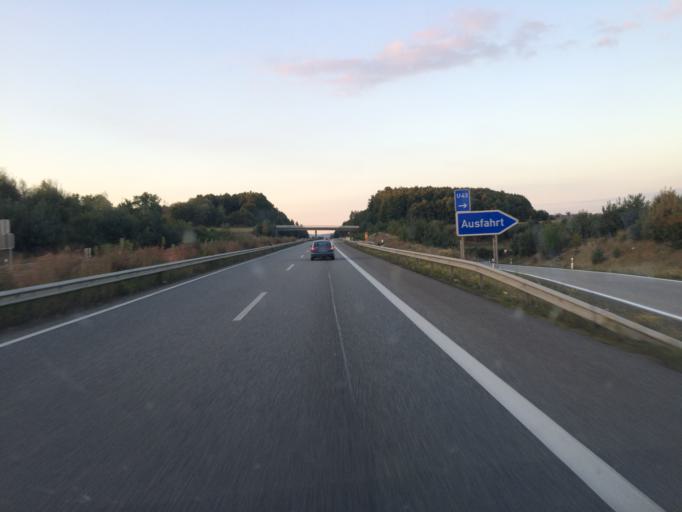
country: DE
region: Rheinland-Pfalz
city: Mehlingen
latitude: 49.5077
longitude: 7.8446
